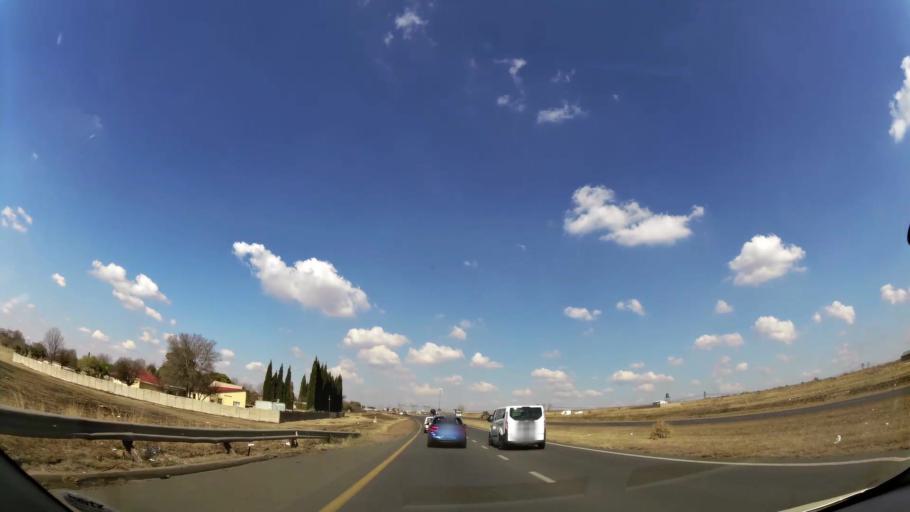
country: ZA
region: Mpumalanga
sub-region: Nkangala District Municipality
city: Witbank
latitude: -25.9327
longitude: 29.2372
